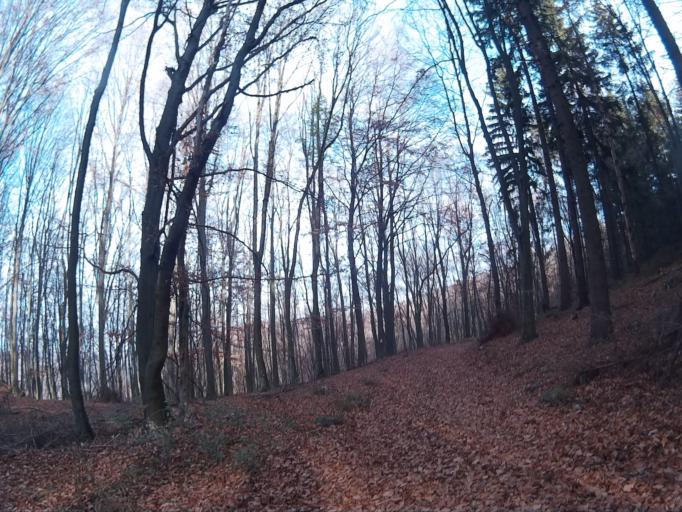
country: HU
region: Heves
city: Belapatfalva
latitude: 48.0519
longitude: 20.3994
